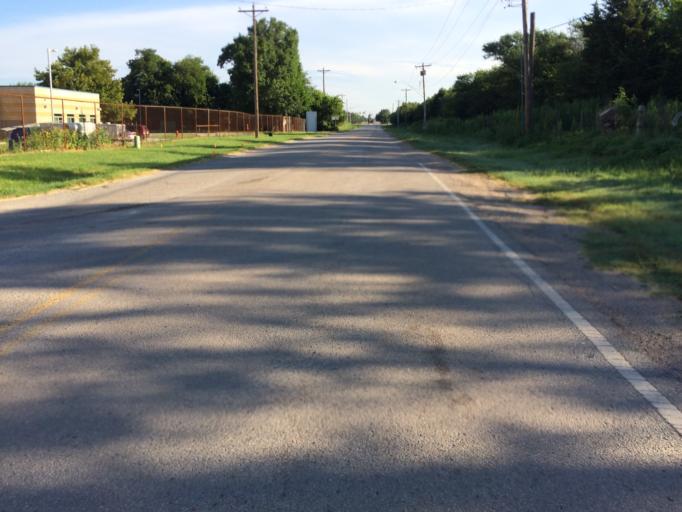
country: US
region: Oklahoma
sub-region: Cleveland County
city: Norman
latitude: 35.1776
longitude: -97.4413
